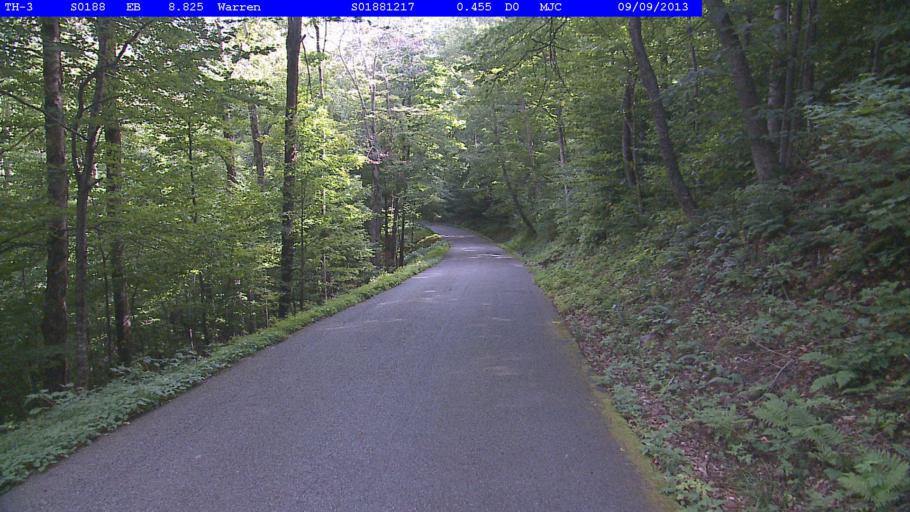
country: US
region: Vermont
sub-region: Addison County
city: Bristol
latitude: 44.0932
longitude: -72.9145
